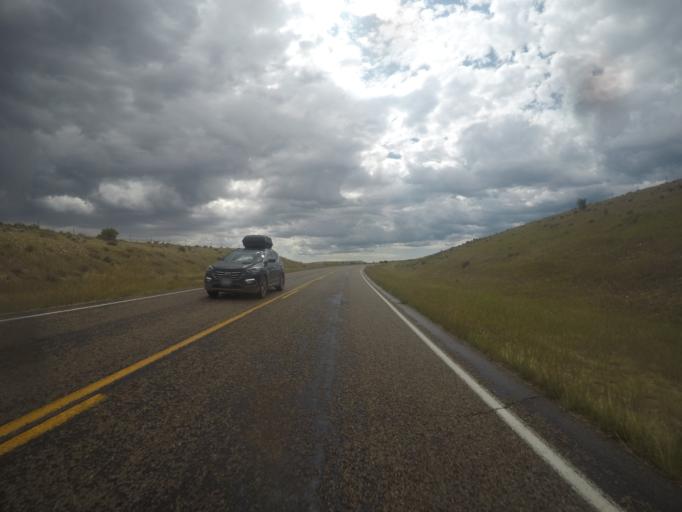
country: US
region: Utah
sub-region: Daggett County
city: Manila
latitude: 41.0269
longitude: -109.8714
